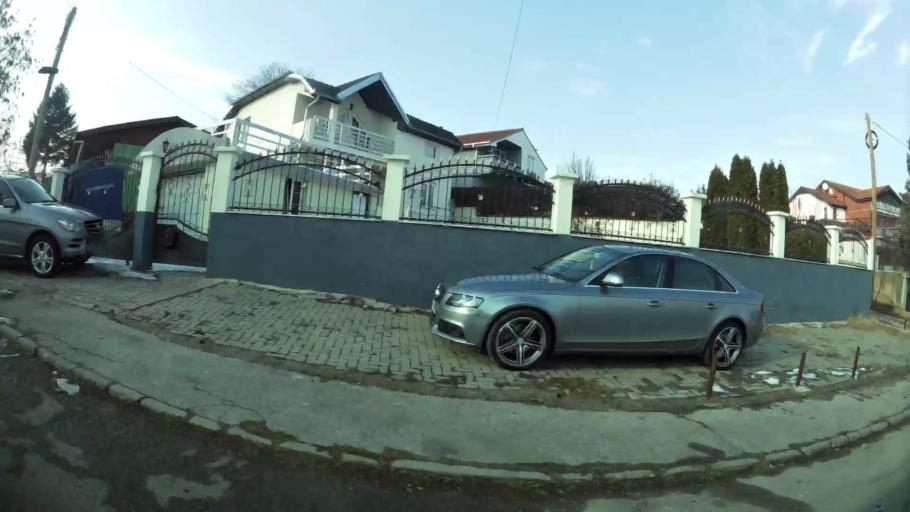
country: MK
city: Creshevo
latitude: 42.0134
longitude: 21.5043
